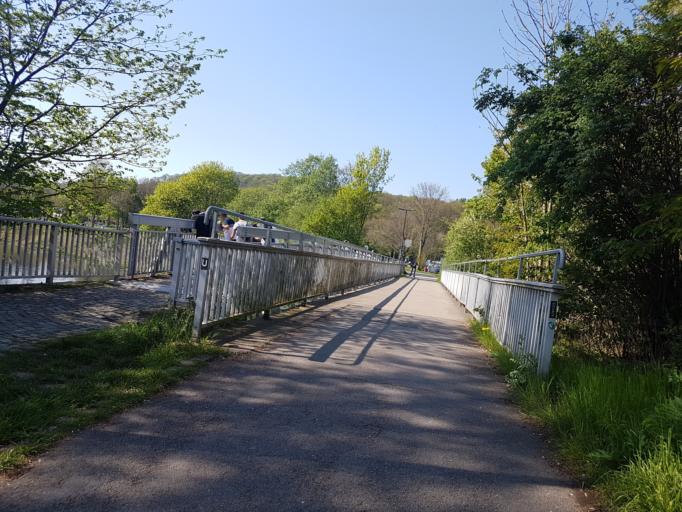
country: DE
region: North Rhine-Westphalia
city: Witten
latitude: 51.4375
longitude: 7.2828
